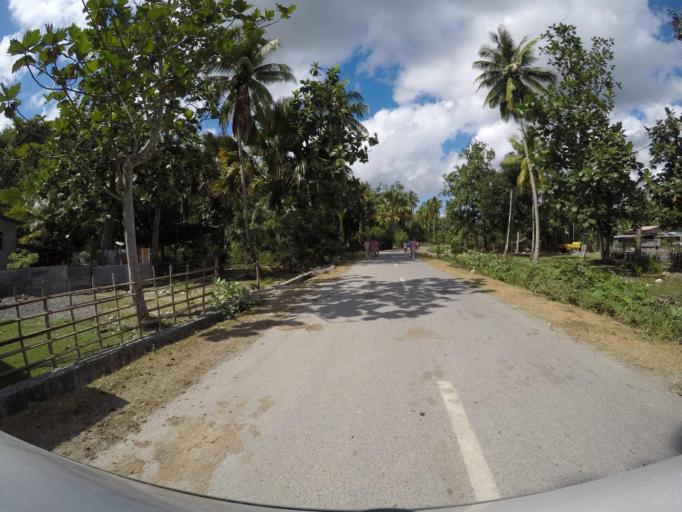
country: TL
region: Viqueque
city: Viqueque
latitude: -8.8615
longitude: 126.3675
